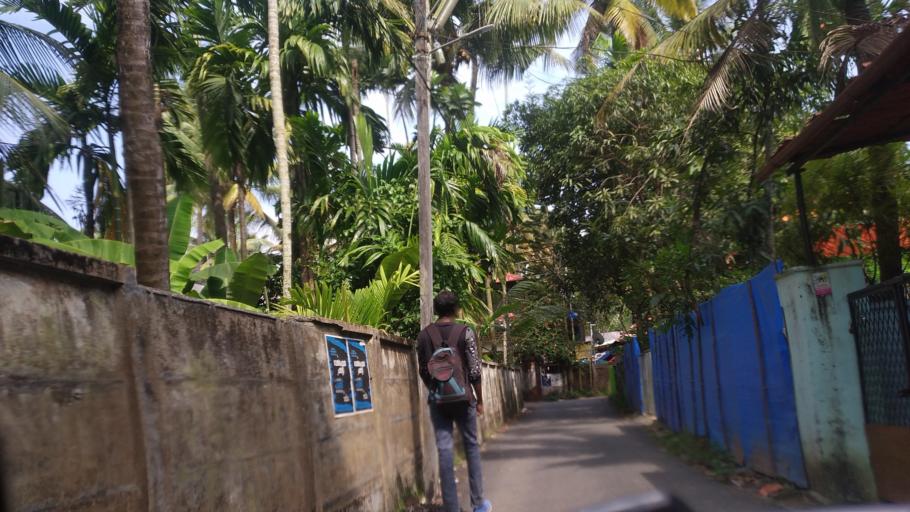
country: IN
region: Kerala
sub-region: Ernakulam
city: Elur
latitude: 10.0882
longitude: 76.2032
